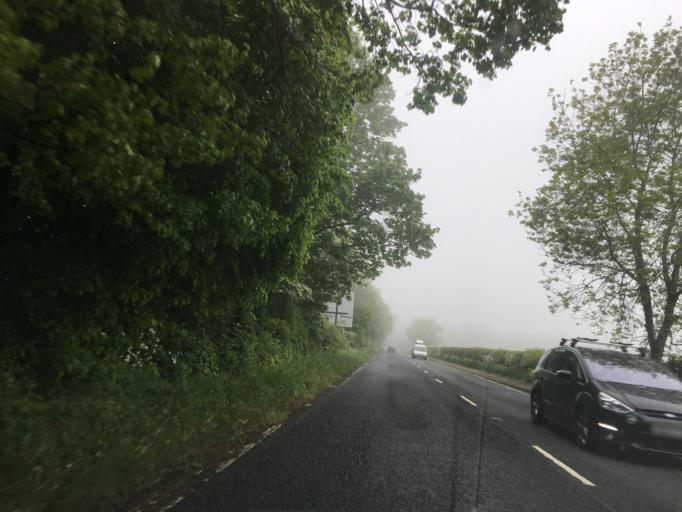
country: GB
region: Scotland
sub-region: Midlothian
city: Loanhead
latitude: 55.8665
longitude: -3.1876
